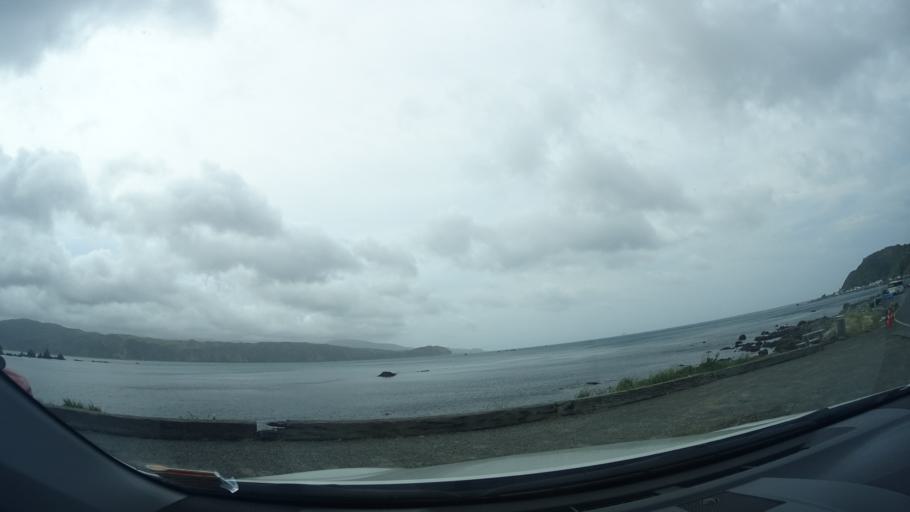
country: NZ
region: Wellington
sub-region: Wellington City
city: Wellington
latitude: -41.3316
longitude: 174.8303
